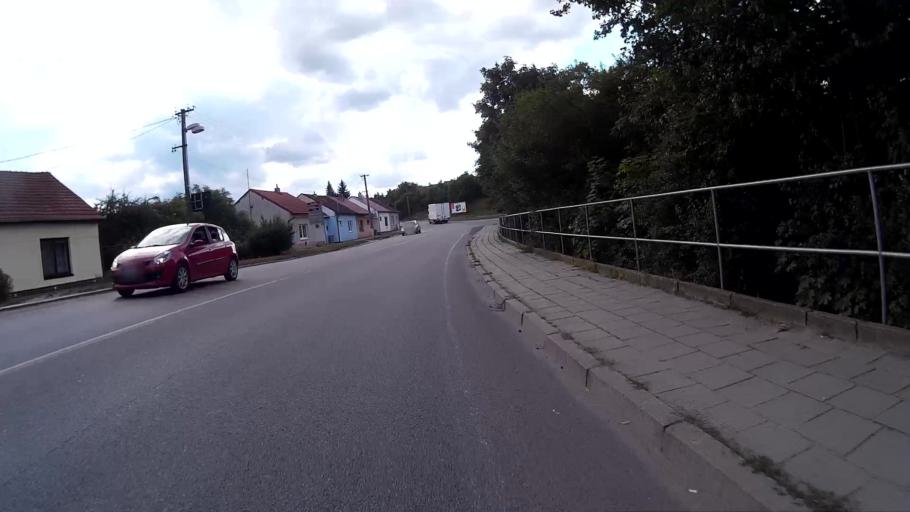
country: CZ
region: South Moravian
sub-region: Okres Brno-Venkov
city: Rosice
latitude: 49.1847
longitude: 16.3849
